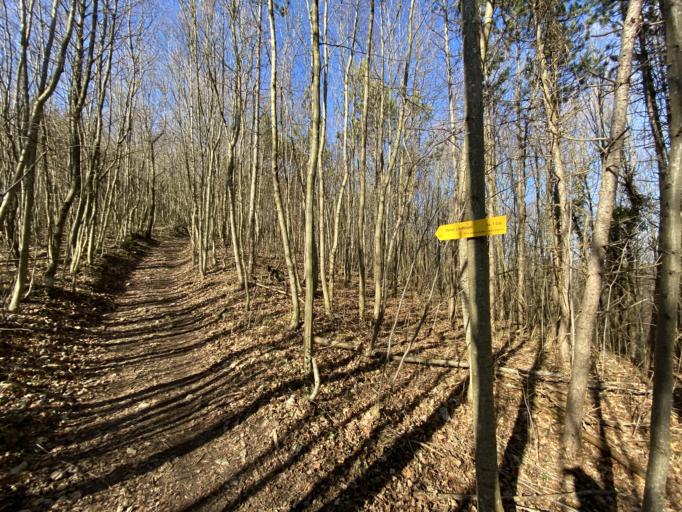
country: AT
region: Lower Austria
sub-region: Politischer Bezirk Baden
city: Heiligenkreuz
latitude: 48.0193
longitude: 16.1608
